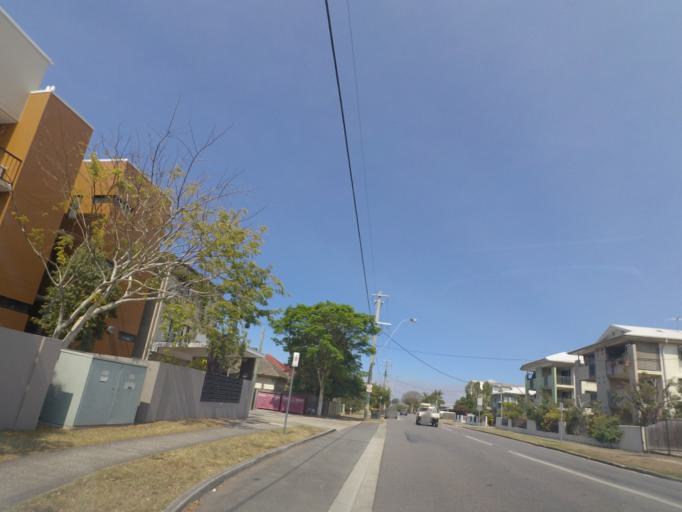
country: AU
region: Queensland
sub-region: Brisbane
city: Upper Mount Gravatt
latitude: -27.5529
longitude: 153.0801
